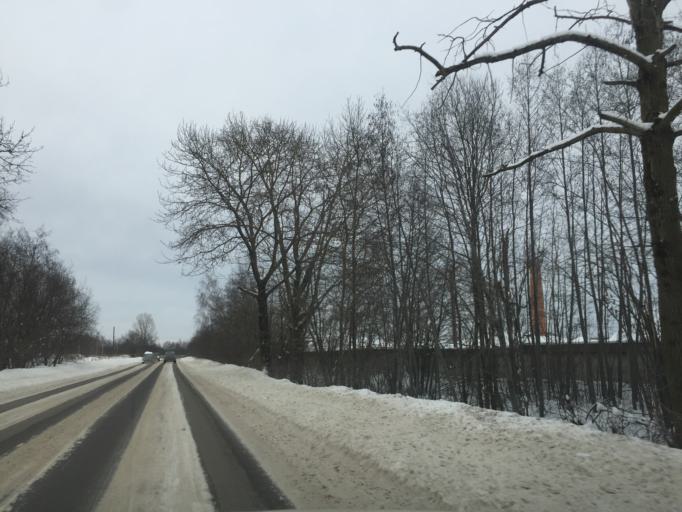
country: RU
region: Leningrad
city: Imeni Sverdlova
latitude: 59.7908
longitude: 30.6922
